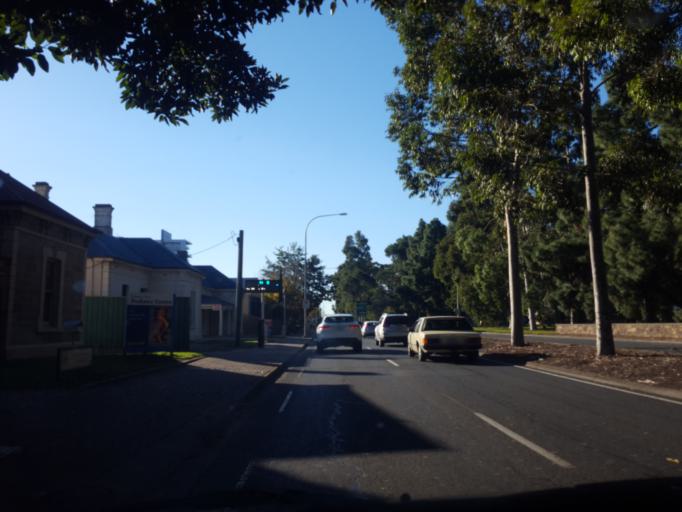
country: AU
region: South Australia
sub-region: Unley
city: Fullarton
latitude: -34.9442
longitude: 138.6248
